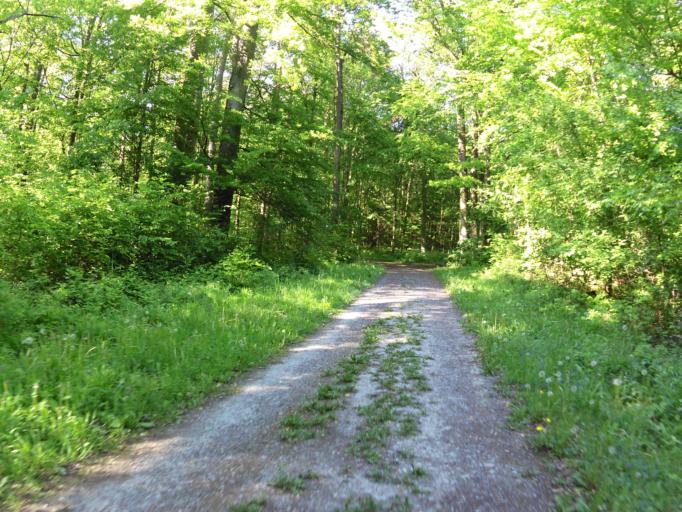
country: DE
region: Bavaria
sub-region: Regierungsbezirk Unterfranken
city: Reichenberg
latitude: 49.7511
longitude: 9.9164
